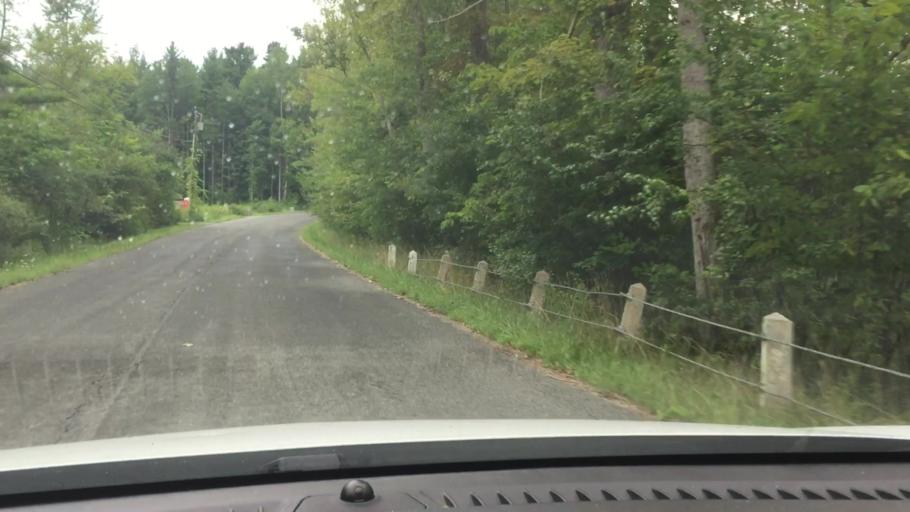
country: US
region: Massachusetts
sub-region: Berkshire County
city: Lee
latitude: 42.3051
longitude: -73.2824
